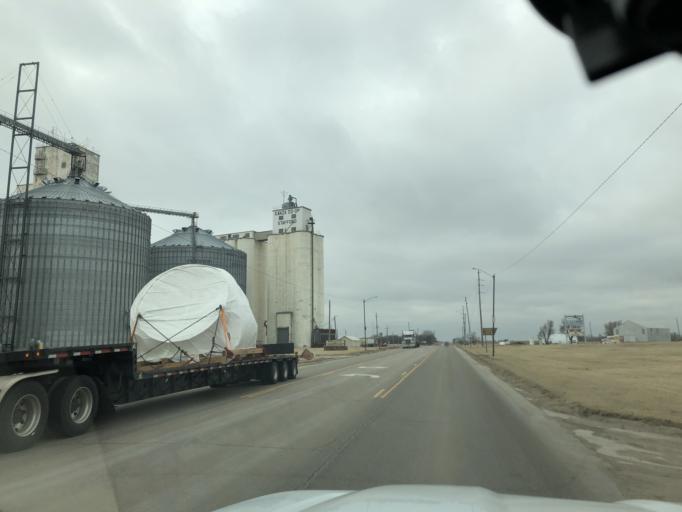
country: US
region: Kansas
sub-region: Stafford County
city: Stafford
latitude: 37.9548
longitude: -98.5974
